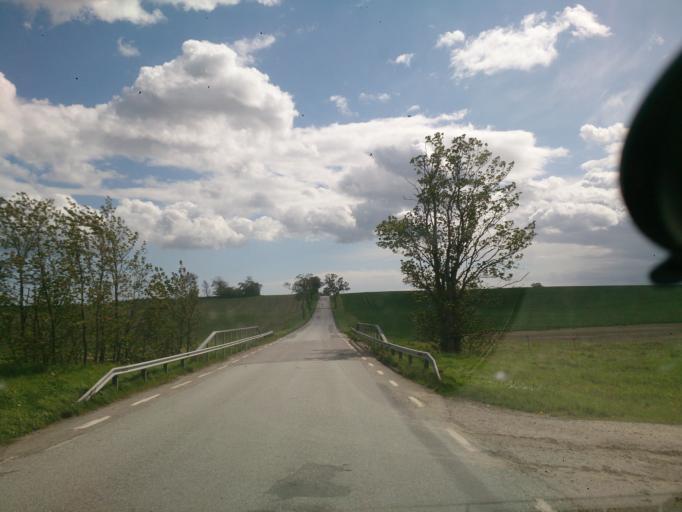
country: SE
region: Skane
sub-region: Ystads Kommun
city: Ystad
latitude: 55.4753
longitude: 13.7090
